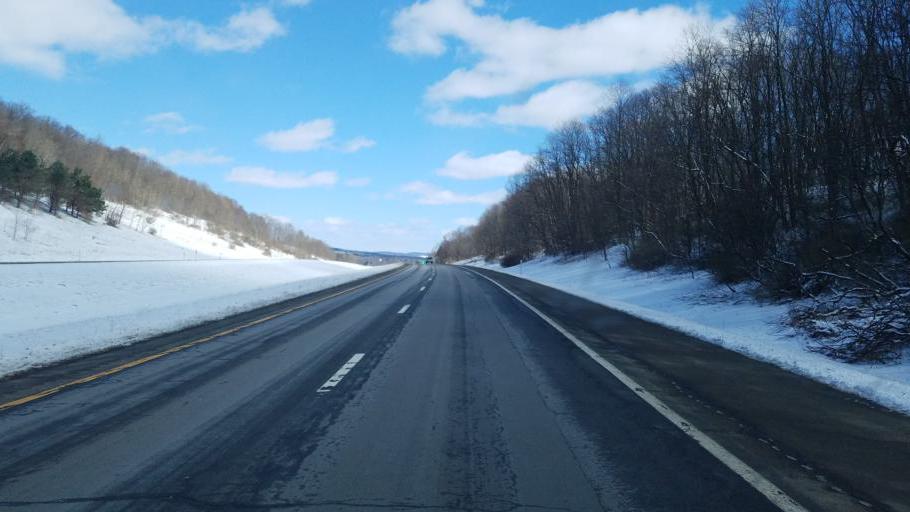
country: US
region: New York
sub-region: Chautauqua County
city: Falconer
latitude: 42.1243
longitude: -79.2155
